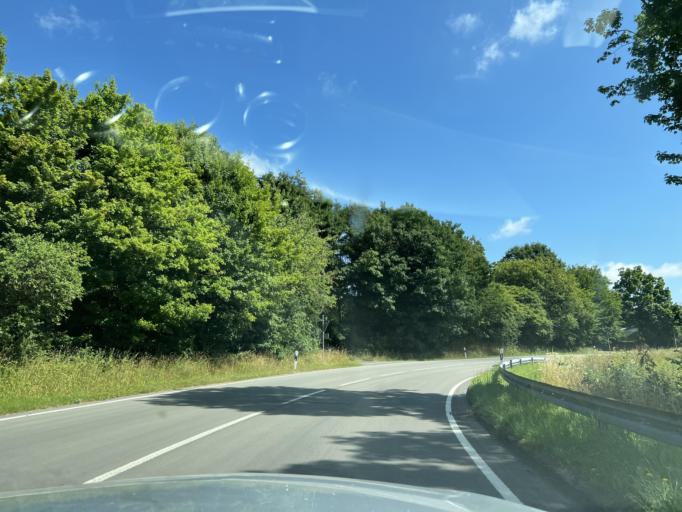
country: DE
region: North Rhine-Westphalia
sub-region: Regierungsbezirk Arnsberg
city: Drolshagen
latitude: 50.9702
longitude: 7.7268
